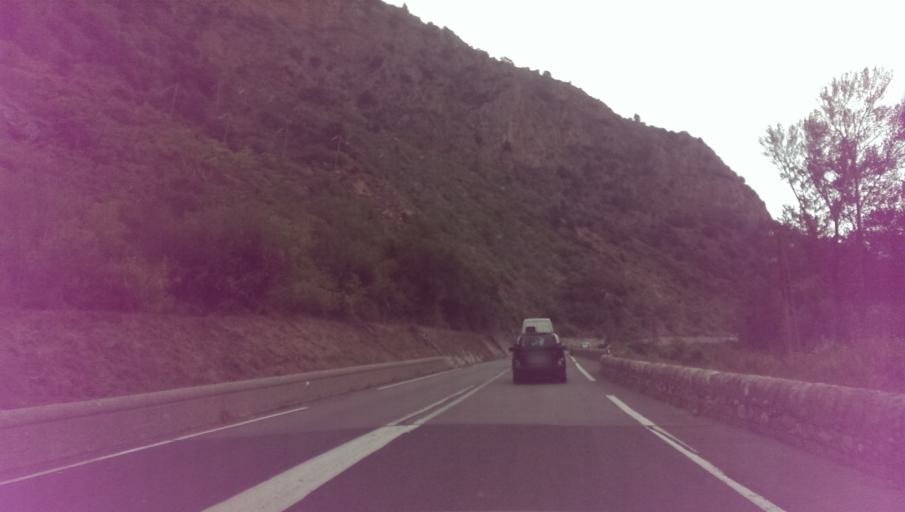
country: FR
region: Languedoc-Roussillon
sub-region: Departement des Pyrenees-Orientales
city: Vernet-les-Bains
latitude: 42.5825
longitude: 2.3538
